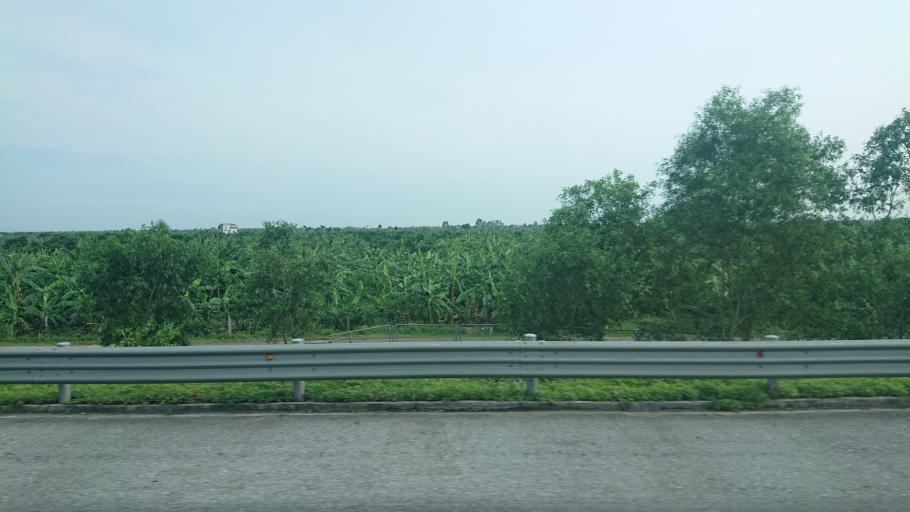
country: VN
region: Hai Duong
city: Tu Ky
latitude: 20.8218
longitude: 106.4738
